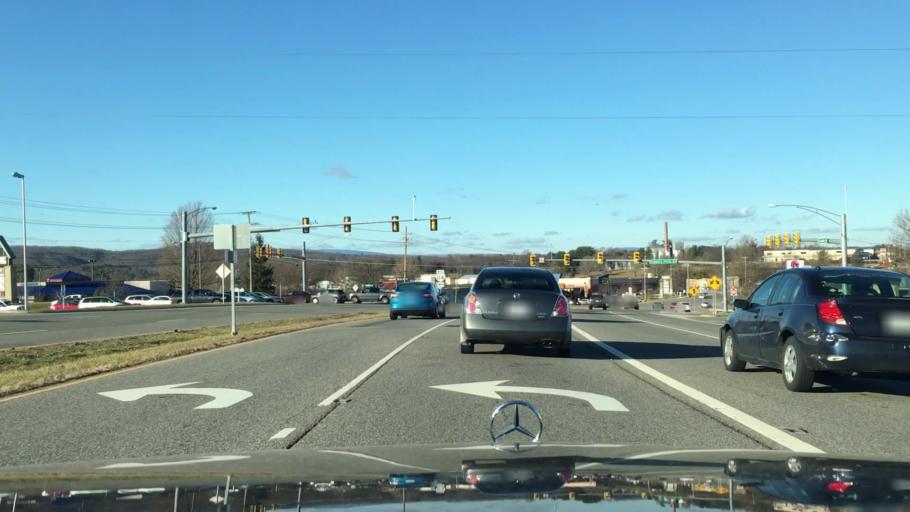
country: US
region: Virginia
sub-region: Montgomery County
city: Merrimac
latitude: 37.1629
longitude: -80.4232
